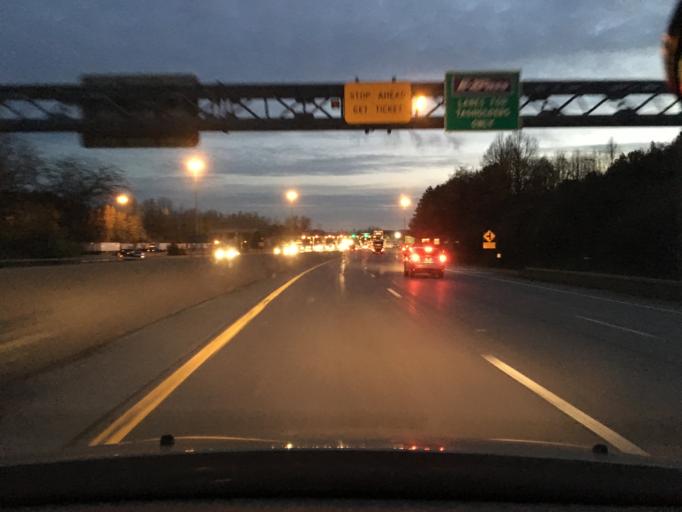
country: US
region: New York
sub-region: Ontario County
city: Victor
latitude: 43.0148
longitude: -77.4395
